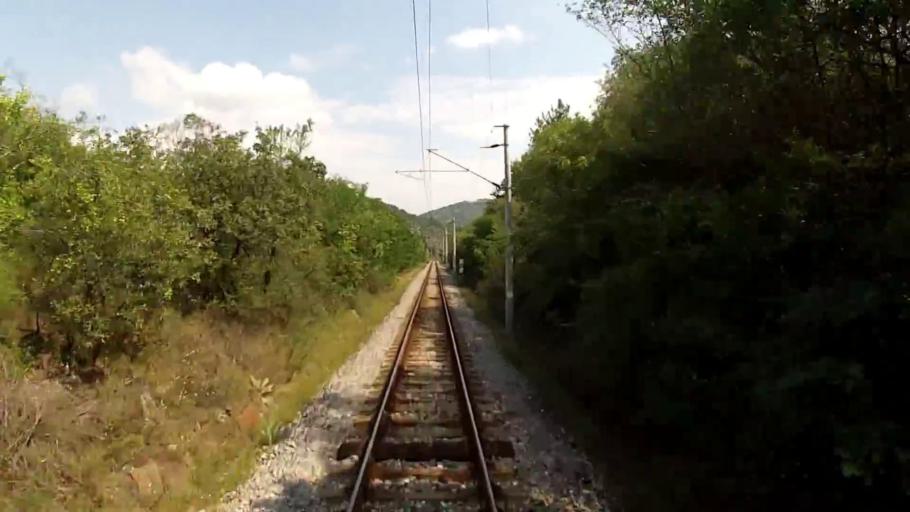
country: BG
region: Blagoevgrad
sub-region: Obshtina Kresna
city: Kresna
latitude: 41.7191
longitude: 23.1647
